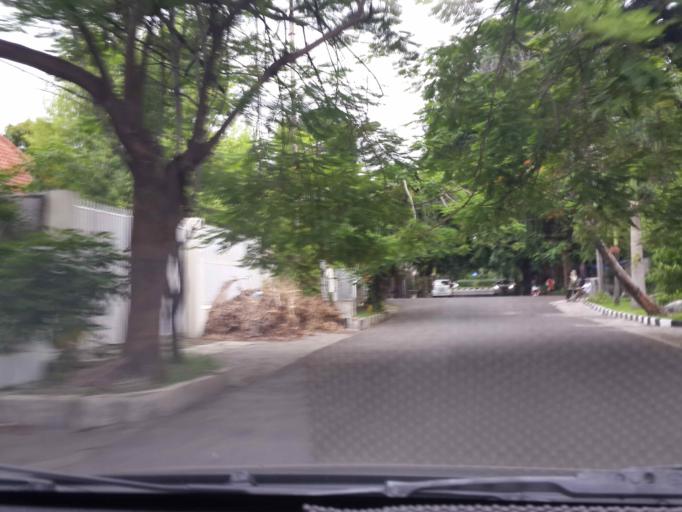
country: ID
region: East Java
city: Gubengairlangga
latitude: -7.2830
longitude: 112.7341
